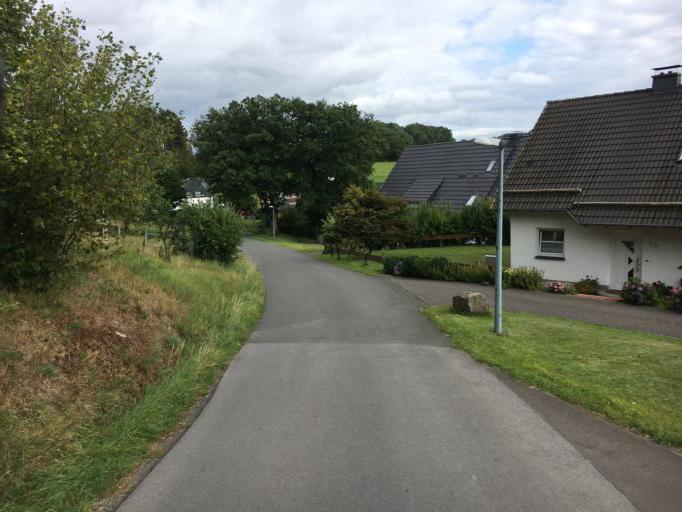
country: DE
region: North Rhine-Westphalia
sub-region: Regierungsbezirk Arnsberg
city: Herscheid
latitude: 51.2045
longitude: 7.7805
